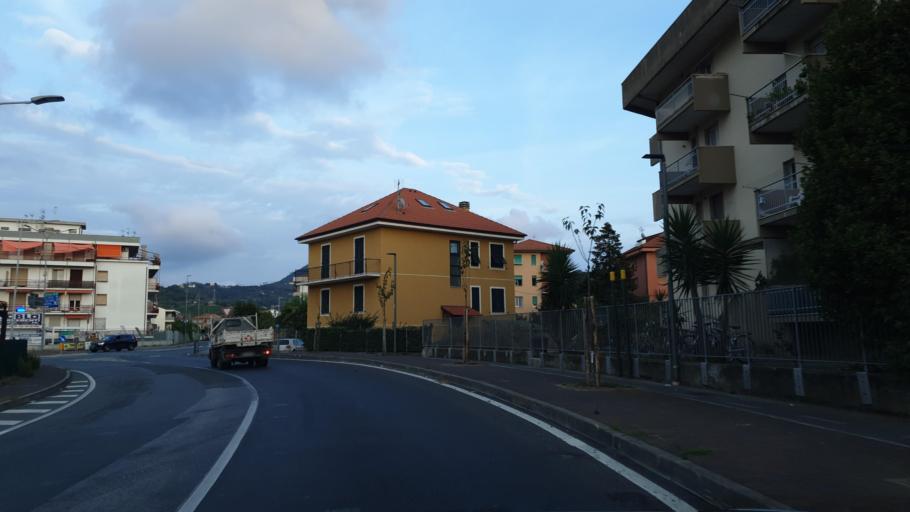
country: IT
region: Liguria
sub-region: Provincia di Genova
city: Sestri Levante
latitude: 44.2689
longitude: 9.4151
